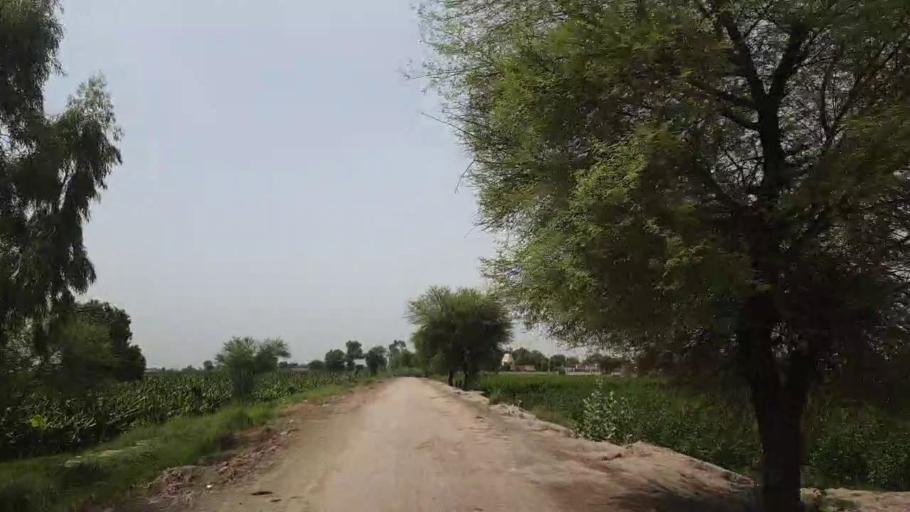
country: PK
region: Sindh
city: Sakrand
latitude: 26.1294
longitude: 68.2865
